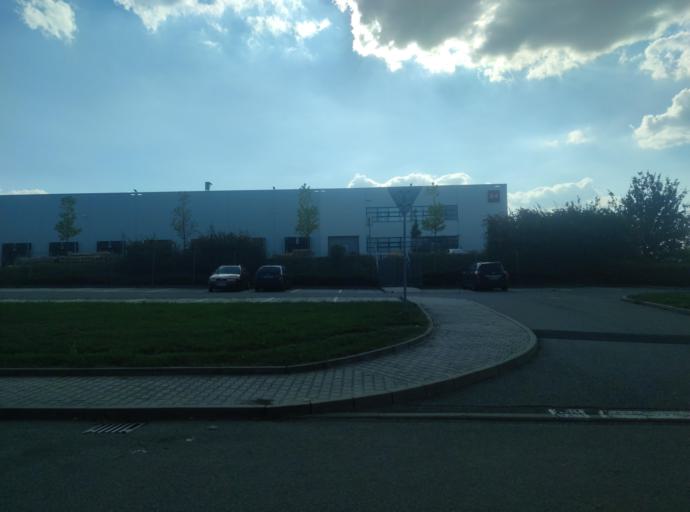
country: CZ
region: South Moravian
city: Podoli
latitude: 49.1693
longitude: 16.6751
